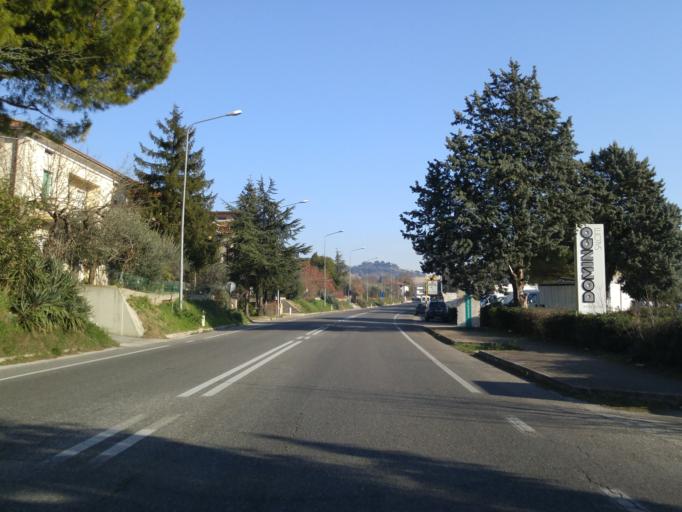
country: IT
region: The Marches
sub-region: Provincia di Pesaro e Urbino
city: Gradara
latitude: 43.9477
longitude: 12.7975
